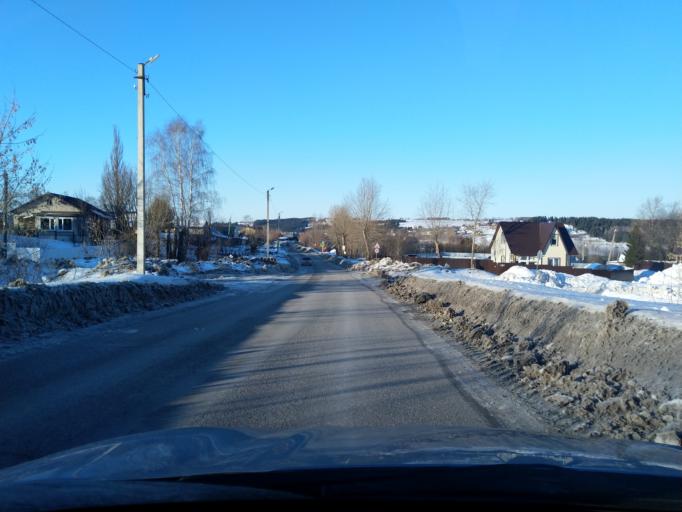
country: RU
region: Perm
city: Polazna
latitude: 58.2942
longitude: 56.4159
